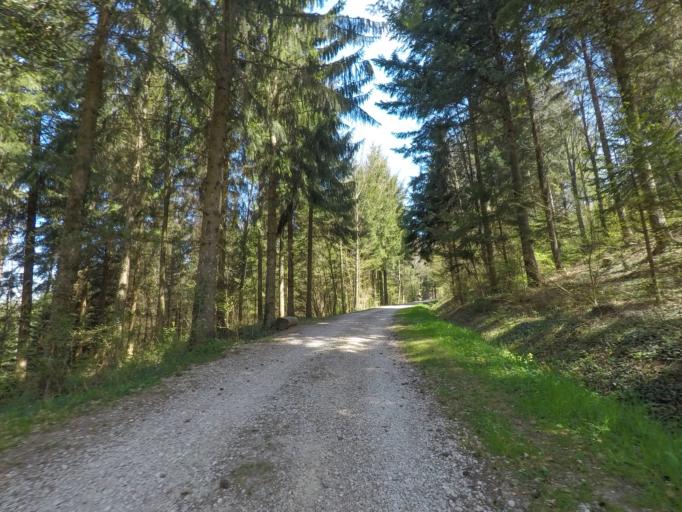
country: FR
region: Rhone-Alpes
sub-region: Departement de la Haute-Savoie
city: Archamps
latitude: 46.1161
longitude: 6.1418
